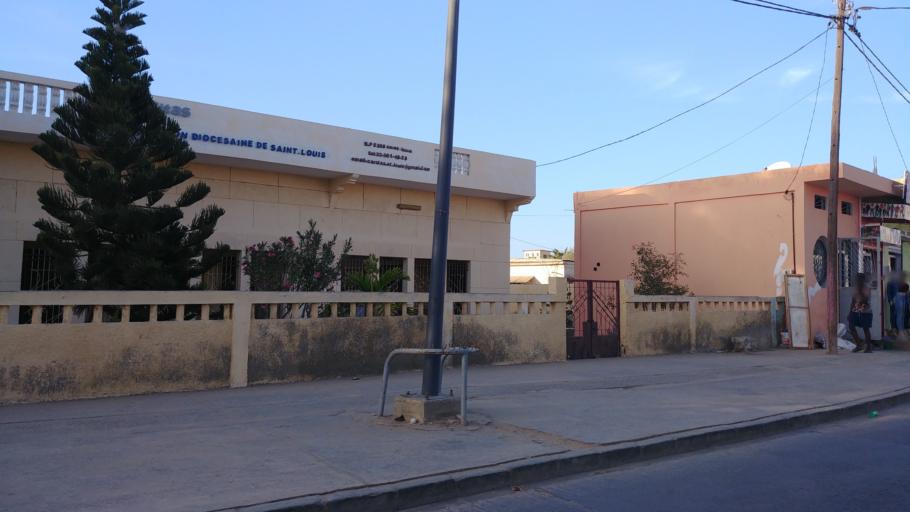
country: SN
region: Saint-Louis
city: Saint-Louis
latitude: 16.0232
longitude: -16.4910
